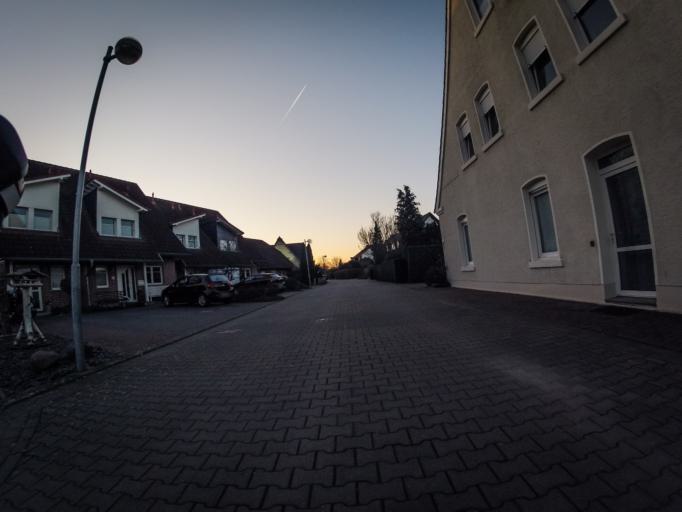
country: DE
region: North Rhine-Westphalia
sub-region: Regierungsbezirk Munster
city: Lotte
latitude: 52.3113
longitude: 7.9364
